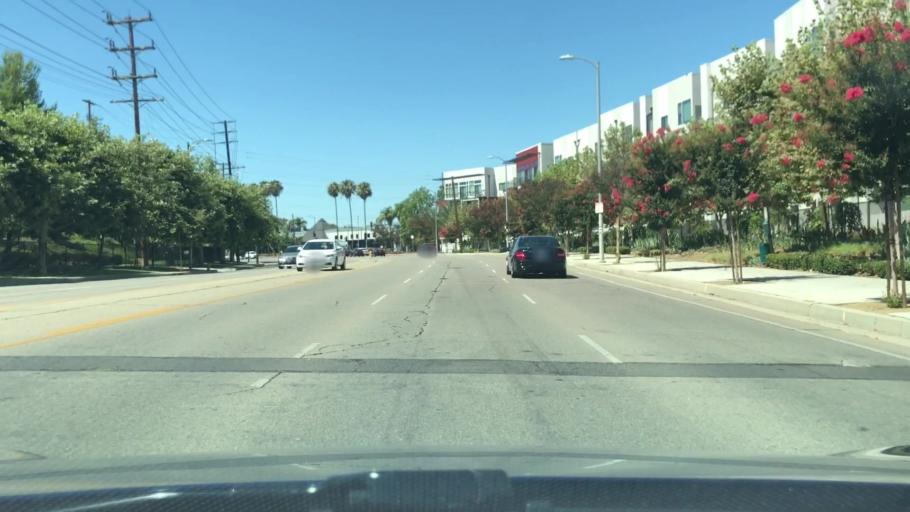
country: US
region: California
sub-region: Los Angeles County
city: Canoga Park
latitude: 34.1840
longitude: -118.5893
